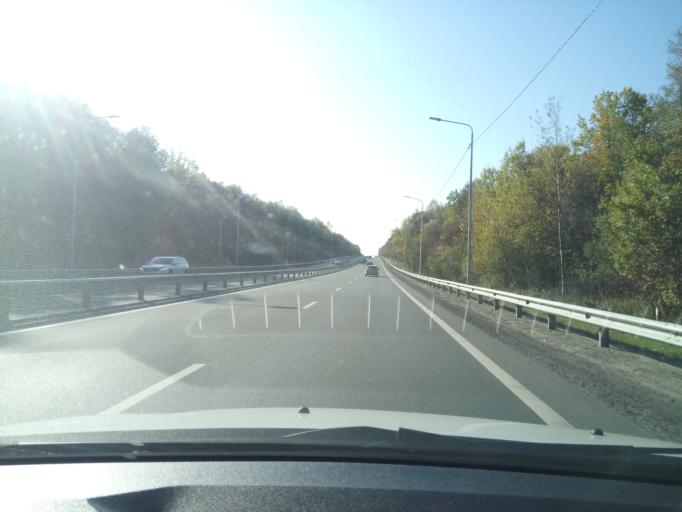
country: RU
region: Nizjnij Novgorod
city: Burevestnik
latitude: 56.0274
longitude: 43.9627
